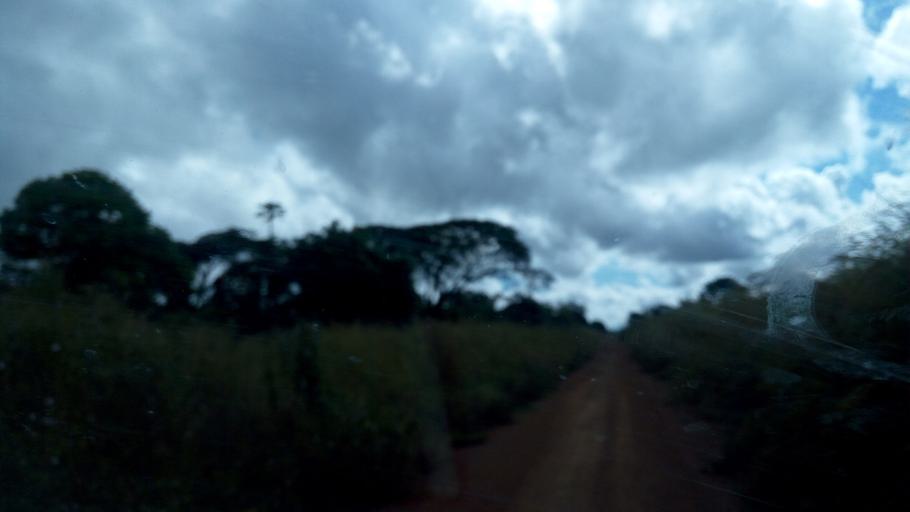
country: ZM
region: Northern
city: Kaputa
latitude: -8.3763
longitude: 28.9602
